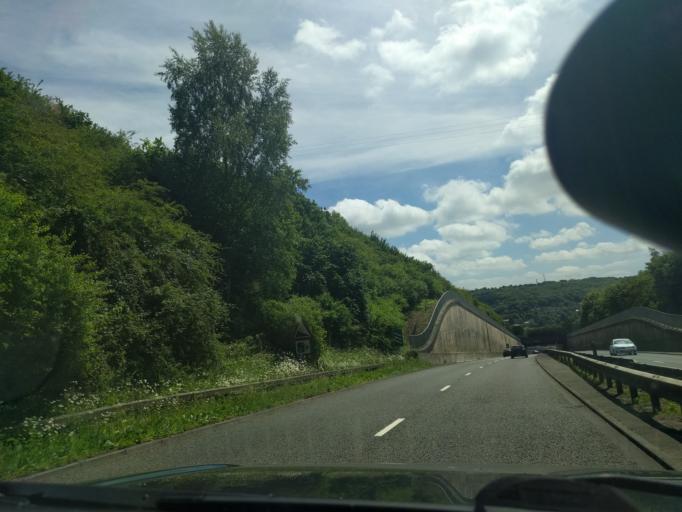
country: GB
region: England
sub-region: Bath and North East Somerset
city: Bath
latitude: 51.4054
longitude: -2.3399
